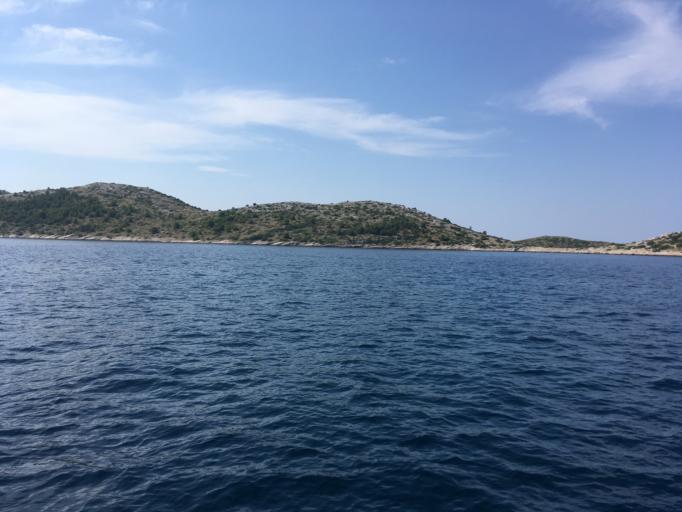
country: HR
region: Zadarska
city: Sali
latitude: 43.8370
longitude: 15.2369
